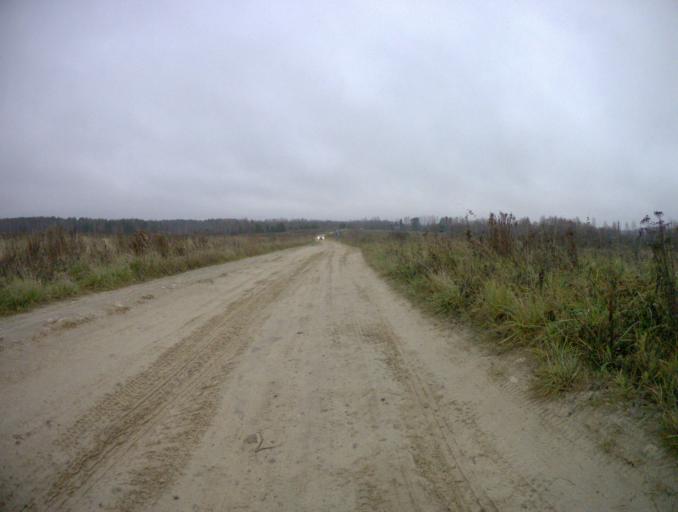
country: RU
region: Vladimir
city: Golovino
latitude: 55.9779
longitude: 40.4559
